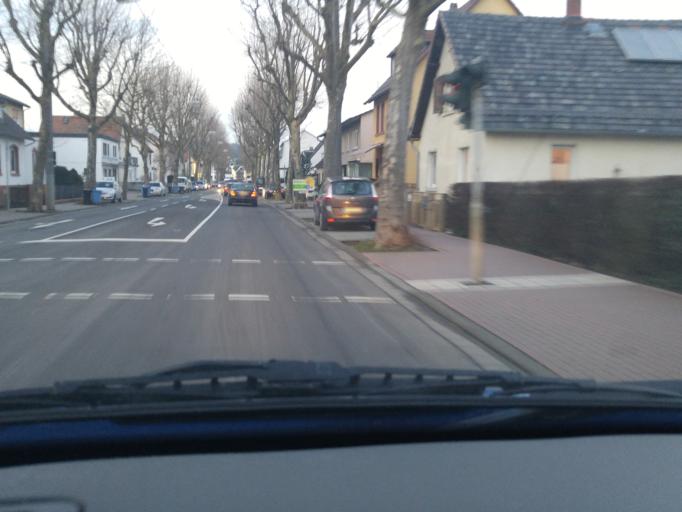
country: DE
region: Hesse
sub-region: Regierungsbezirk Darmstadt
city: Friedrichsdorf
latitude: 50.2719
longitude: 8.6491
